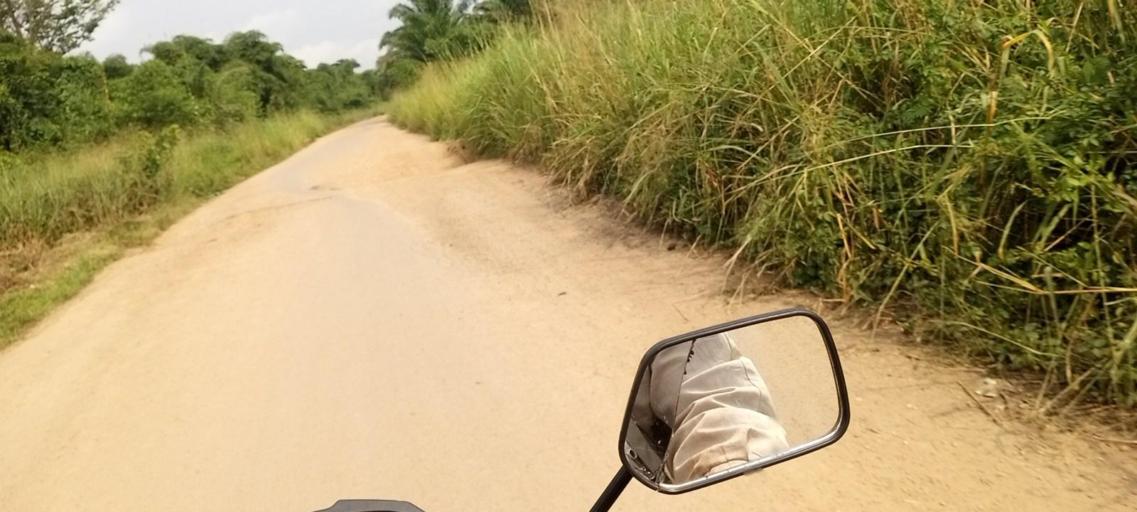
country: CD
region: Eastern Province
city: Kisangani
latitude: 0.3243
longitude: 25.4288
